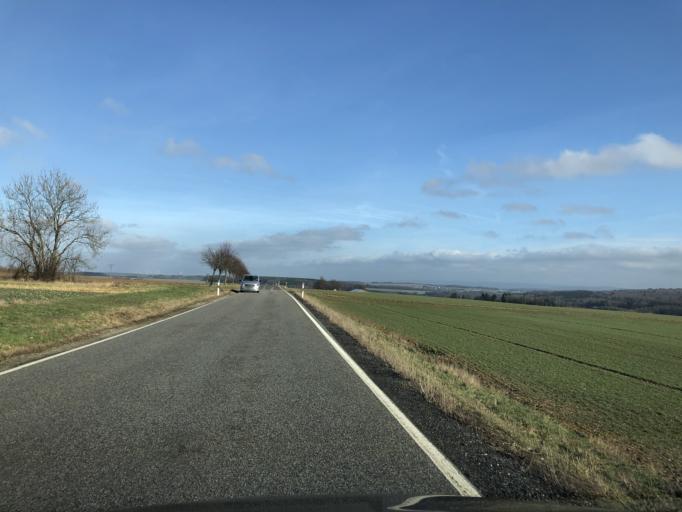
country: DE
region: Rheinland-Pfalz
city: Hochscheid
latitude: 49.8832
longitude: 7.2247
